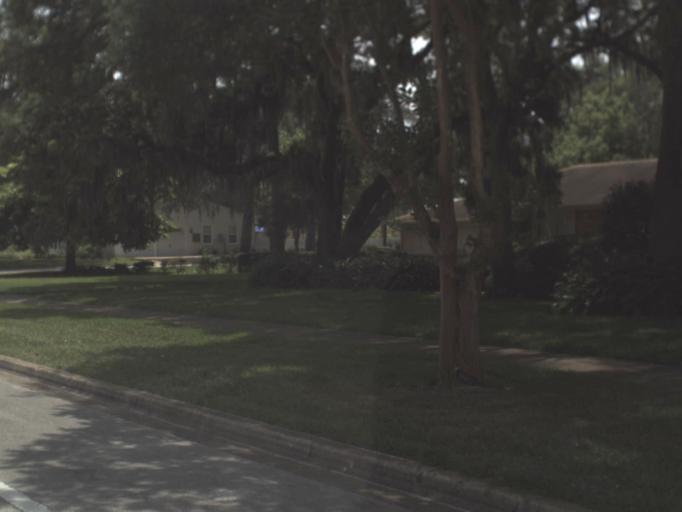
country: US
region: Florida
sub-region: Nassau County
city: Fernandina Beach
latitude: 30.6695
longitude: -81.4482
